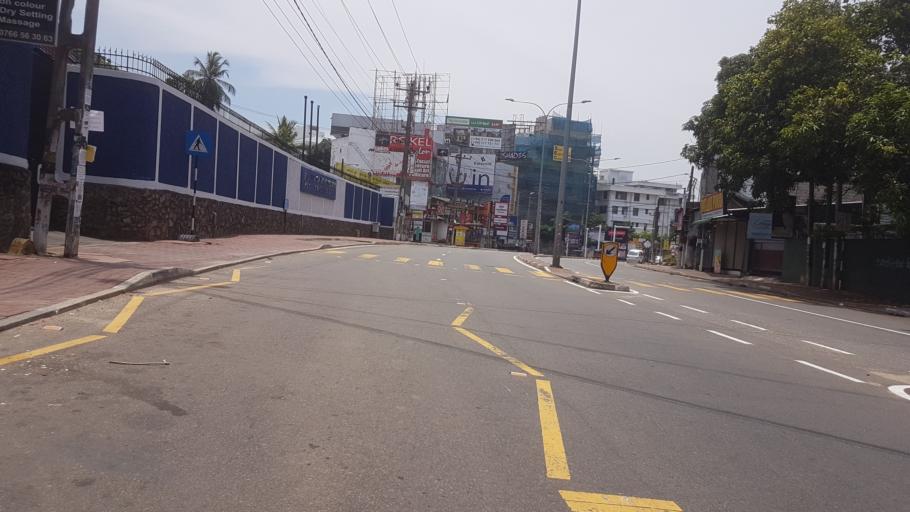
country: LK
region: Western
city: Battaramulla South
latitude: 6.8925
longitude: 79.9285
